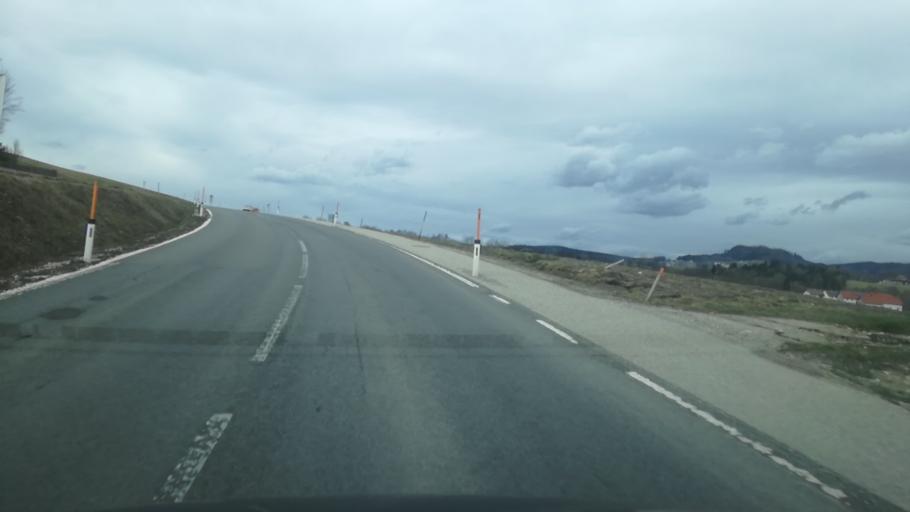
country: AT
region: Upper Austria
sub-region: Politischer Bezirk Vocklabruck
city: Frankenburg
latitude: 48.0468
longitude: 13.4867
